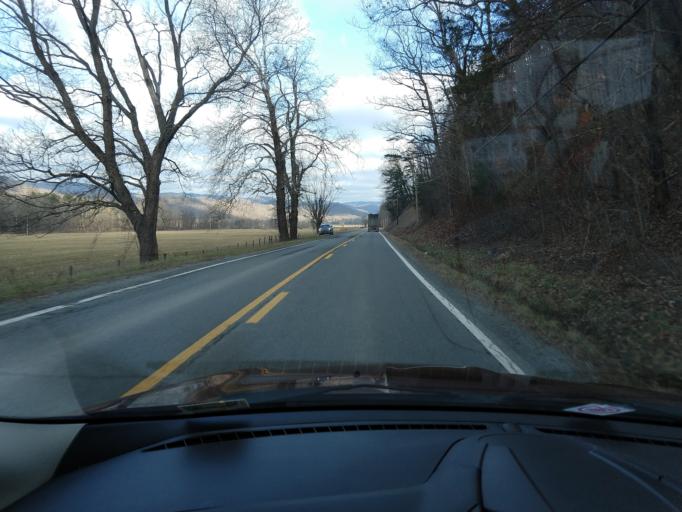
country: US
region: West Virginia
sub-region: Randolph County
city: Elkins
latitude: 38.6846
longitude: -79.9738
